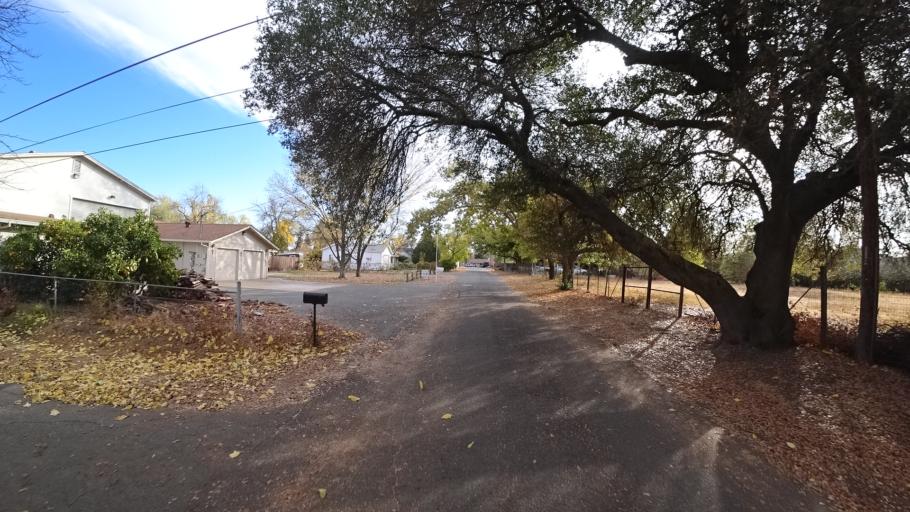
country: US
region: California
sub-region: Sacramento County
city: Citrus Heights
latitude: 38.7019
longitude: -121.2665
